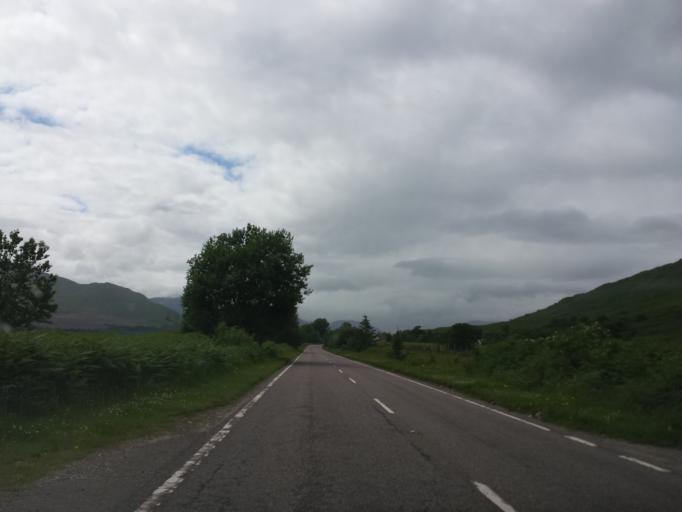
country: GB
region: Scotland
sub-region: Highland
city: Fort William
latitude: 56.8553
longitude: -5.2782
